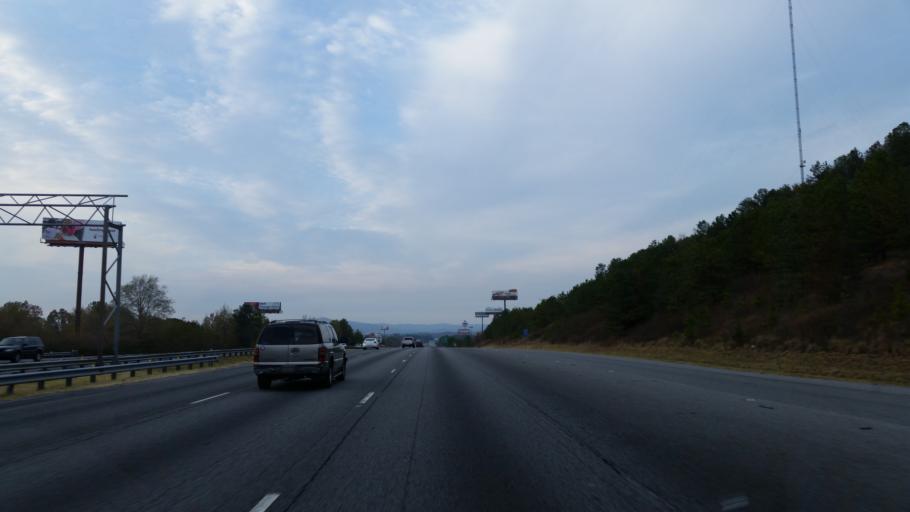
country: US
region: Georgia
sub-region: Gordon County
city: Calhoun
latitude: 34.5455
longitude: -84.9247
